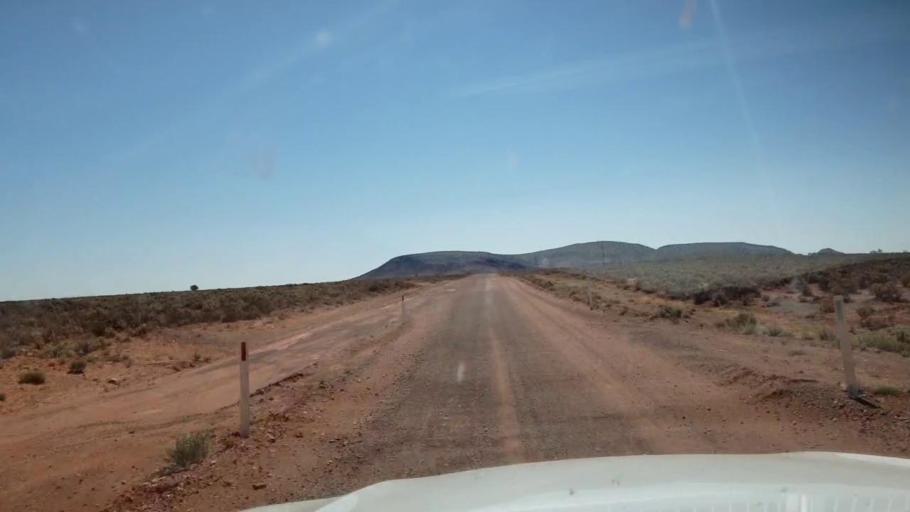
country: AU
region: South Australia
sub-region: Whyalla
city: Whyalla
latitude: -32.7082
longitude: 137.1387
